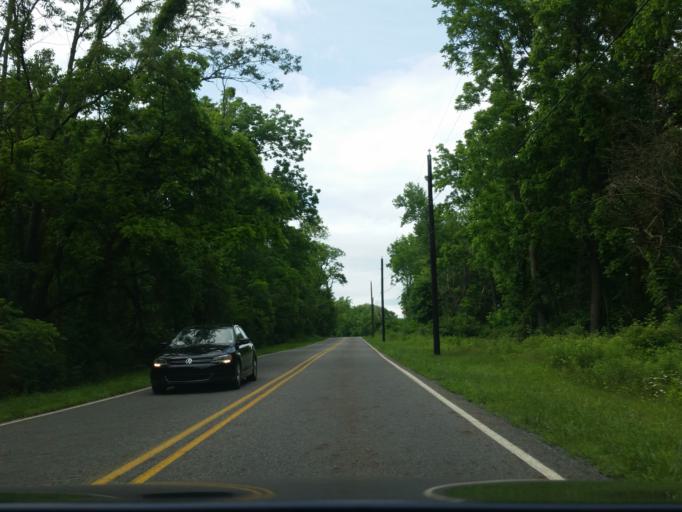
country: US
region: Pennsylvania
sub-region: Lebanon County
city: Jonestown
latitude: 40.4282
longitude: -76.5415
